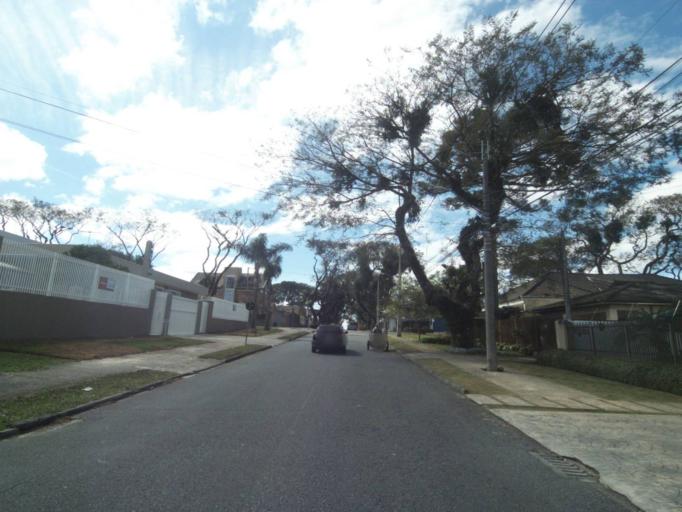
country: BR
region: Parana
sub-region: Curitiba
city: Curitiba
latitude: -25.4564
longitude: -49.2749
